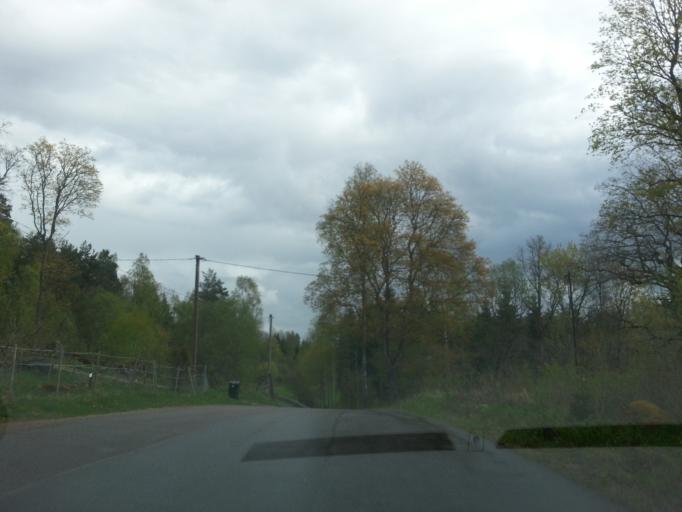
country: SE
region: OEstergoetland
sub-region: Norrkopings Kommun
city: Jursla
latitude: 58.6878
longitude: 16.2411
